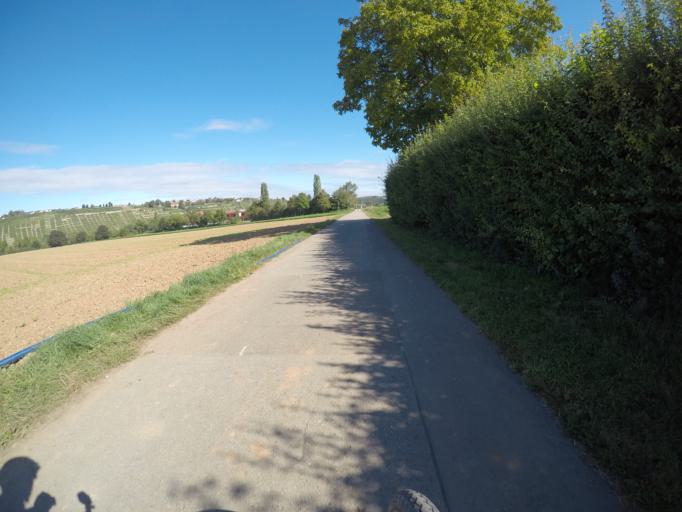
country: DE
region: Baden-Wuerttemberg
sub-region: Regierungsbezirk Stuttgart
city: Pleidelsheim
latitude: 48.9663
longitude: 9.2023
